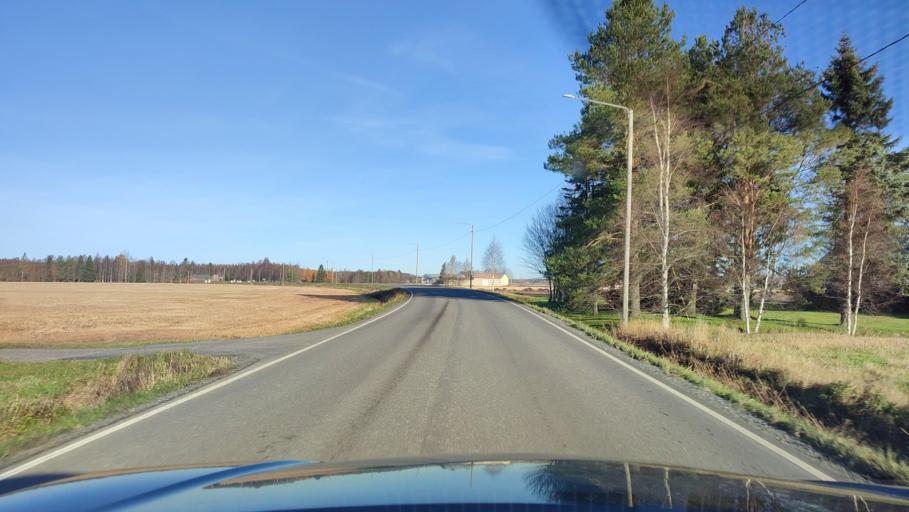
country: FI
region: Southern Ostrobothnia
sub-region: Suupohja
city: Karijoki
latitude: 62.2967
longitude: 21.7202
